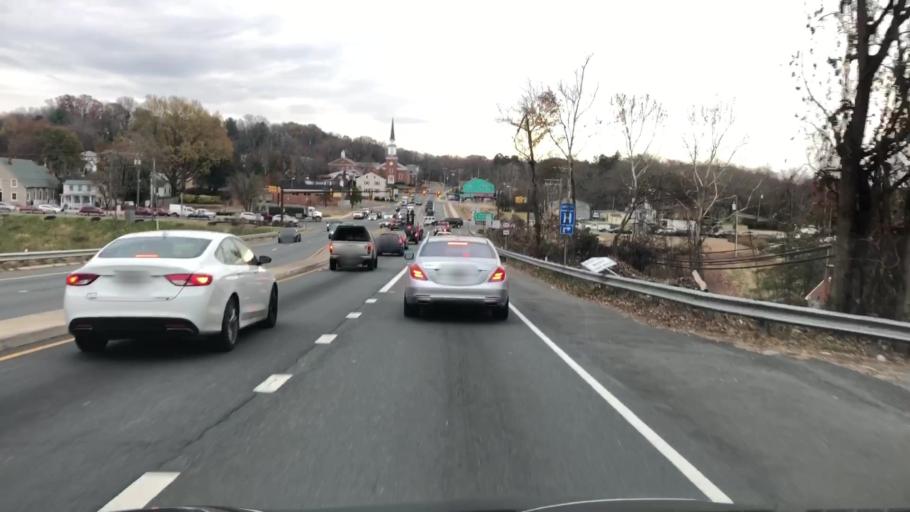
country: US
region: Virginia
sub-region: Stafford County
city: Falmouth
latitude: 38.3247
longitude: -77.4702
